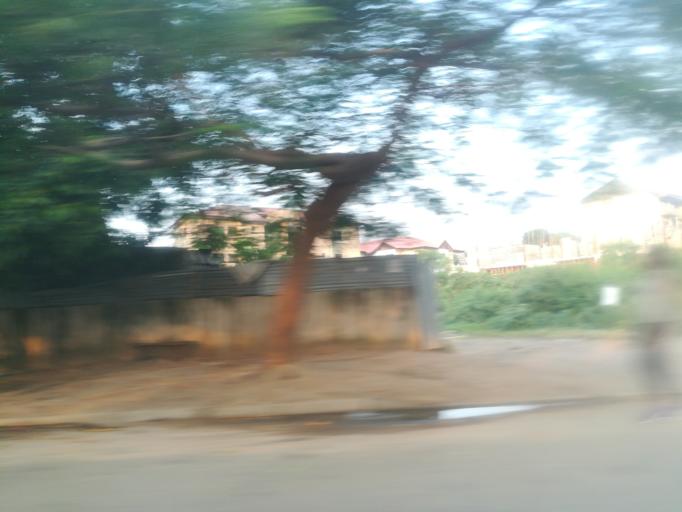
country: NG
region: Abuja Federal Capital Territory
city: Abuja
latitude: 9.0639
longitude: 7.4410
